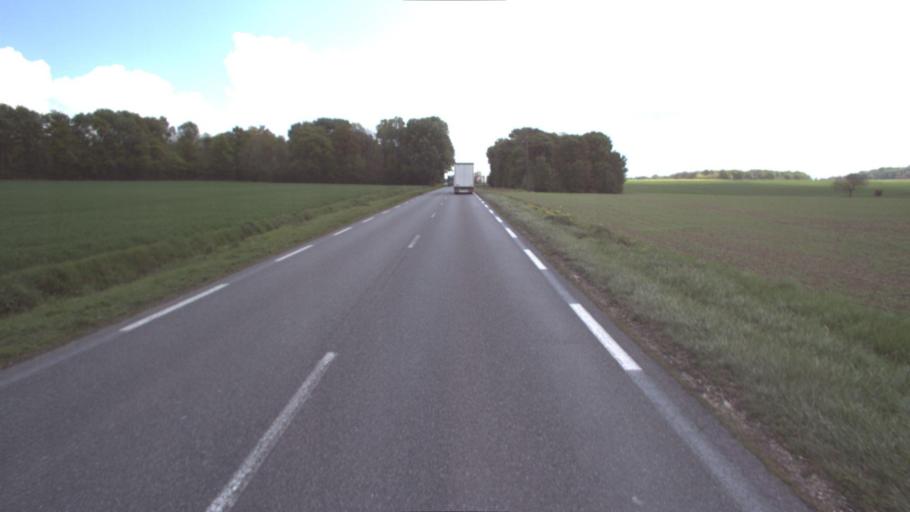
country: FR
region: Ile-de-France
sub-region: Departement de Seine-et-Marne
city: Jouy-le-Chatel
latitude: 48.6916
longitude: 3.1604
